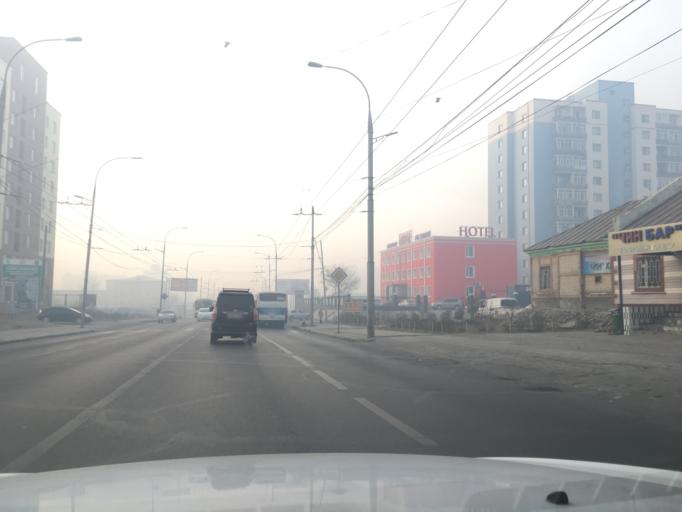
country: MN
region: Ulaanbaatar
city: Ulaanbaatar
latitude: 47.9162
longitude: 106.8183
